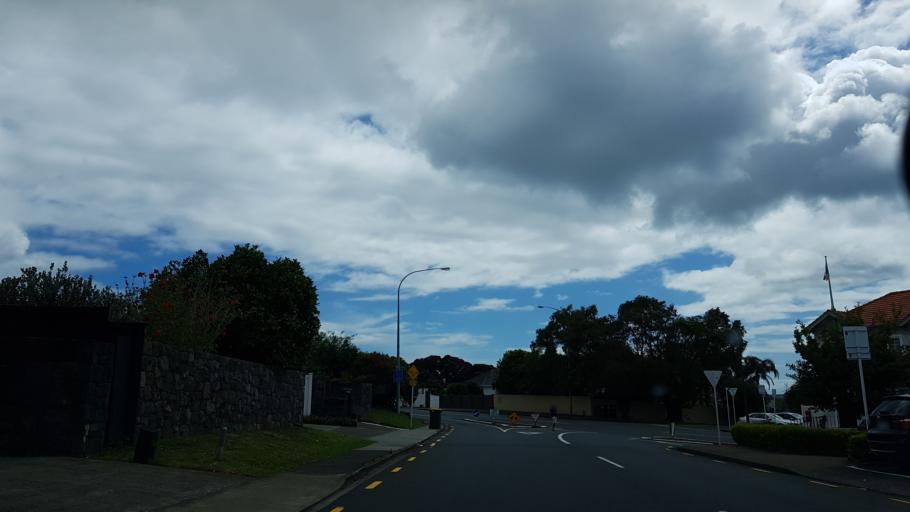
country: NZ
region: Auckland
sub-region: Auckland
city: North Shore
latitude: -36.7828
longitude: 174.7733
